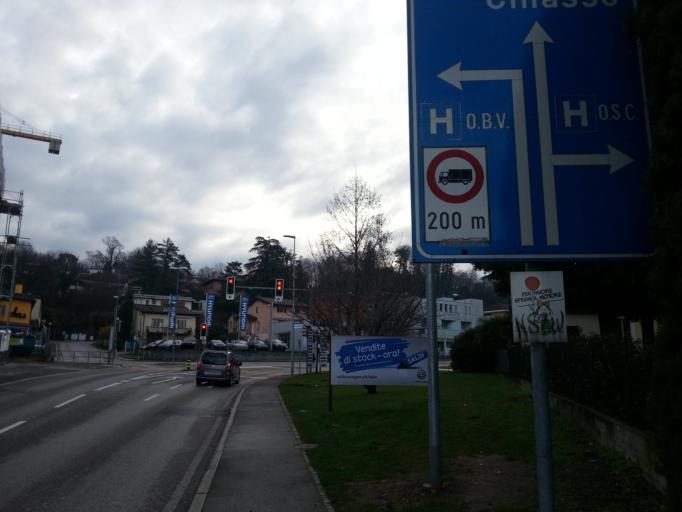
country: CH
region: Ticino
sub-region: Mendrisio District
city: Mendrisio
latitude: 45.8645
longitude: 8.9812
